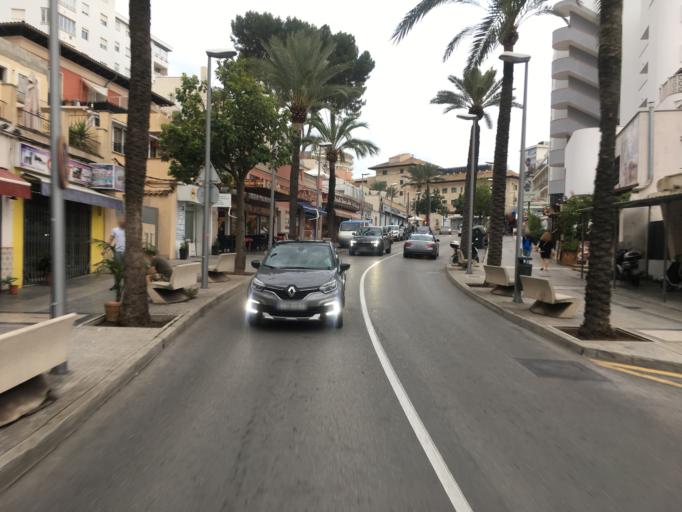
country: ES
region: Balearic Islands
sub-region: Illes Balears
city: Palma
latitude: 39.5536
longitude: 2.6060
